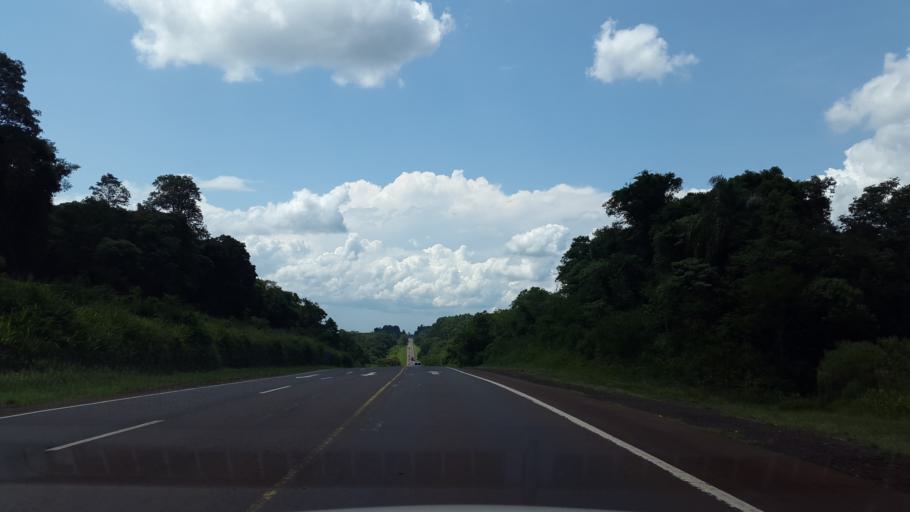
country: AR
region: Misiones
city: El Alcazar
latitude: -26.7113
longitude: -54.8483
